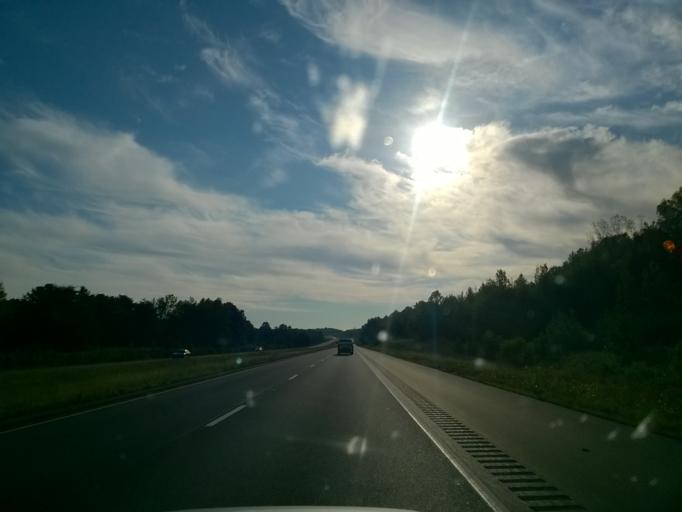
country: US
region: Indiana
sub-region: Warrick County
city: Boonville
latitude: 38.1922
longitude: -87.3139
